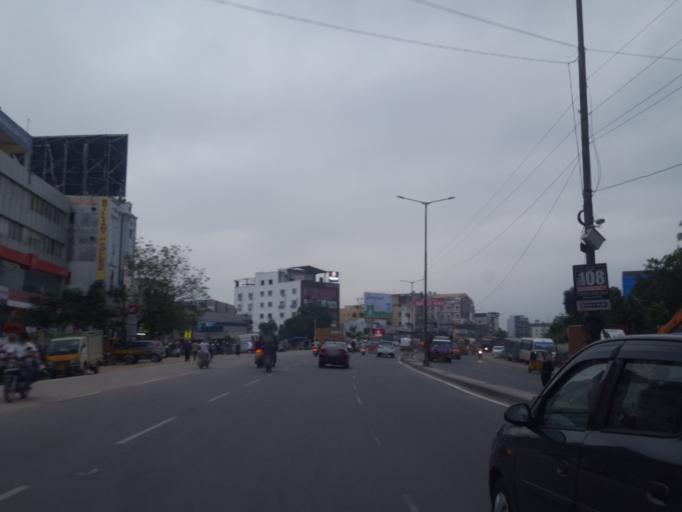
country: IN
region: Telangana
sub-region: Medak
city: Serilingampalle
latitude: 17.5034
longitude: 78.3106
